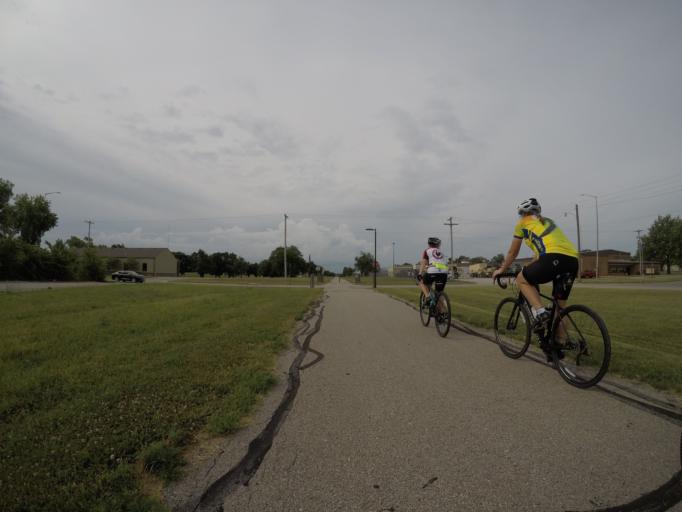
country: US
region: Kansas
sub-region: Franklin County
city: Ottawa
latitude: 38.5906
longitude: -95.2705
